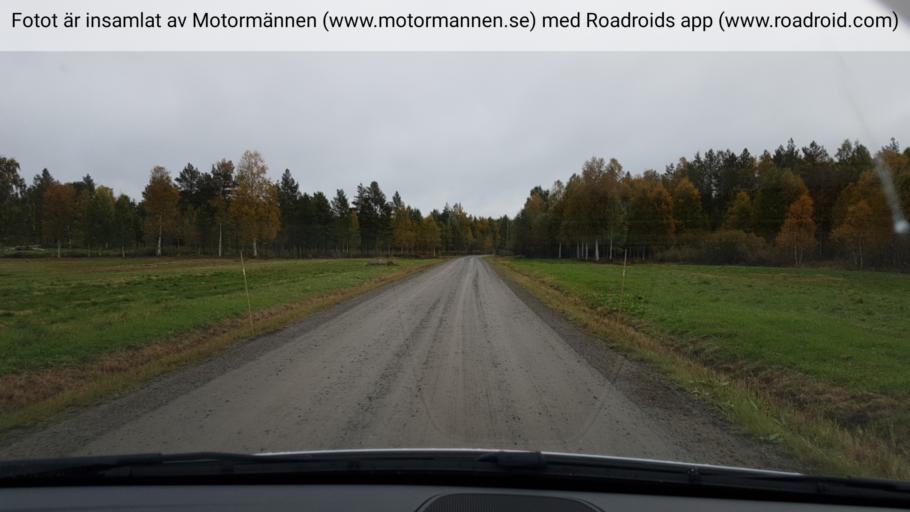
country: SE
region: Vaesterbotten
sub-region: Umea Kommun
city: Ersmark
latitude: 64.1164
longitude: 20.3608
